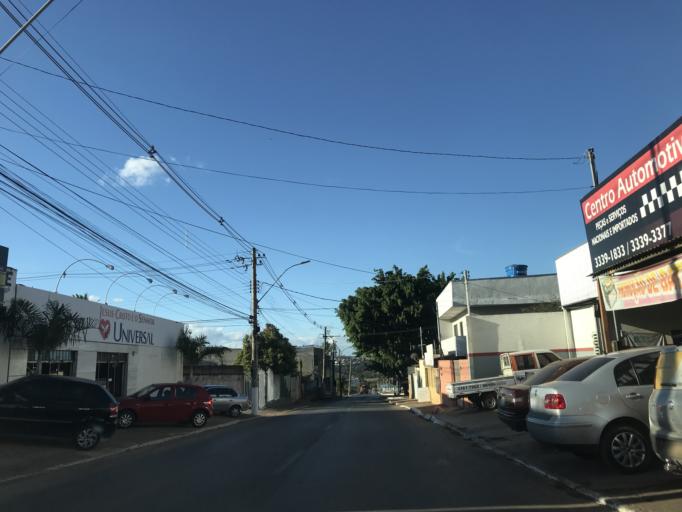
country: BR
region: Federal District
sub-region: Brasilia
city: Brasilia
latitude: -15.8950
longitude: -47.7853
